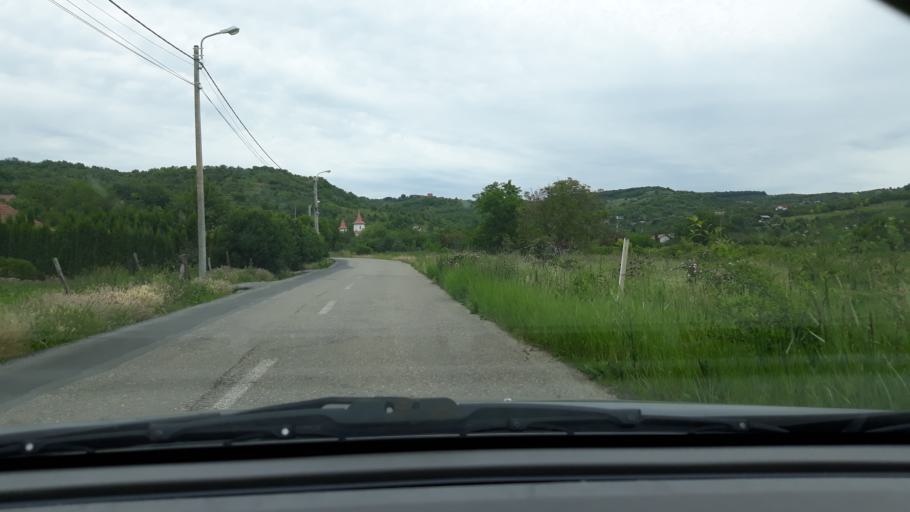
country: RO
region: Bihor
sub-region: Comuna Osorheiu
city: Alparea
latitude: 47.0559
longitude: 22.0016
